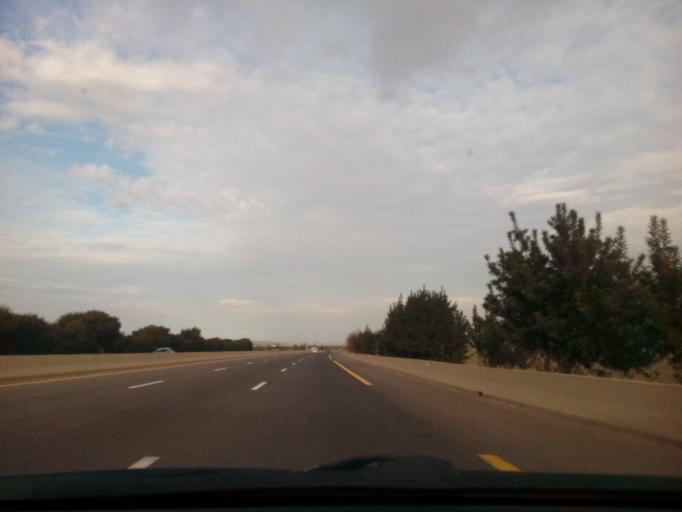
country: DZ
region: Mostaganem
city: Mostaganem
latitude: 35.6818
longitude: 0.1552
